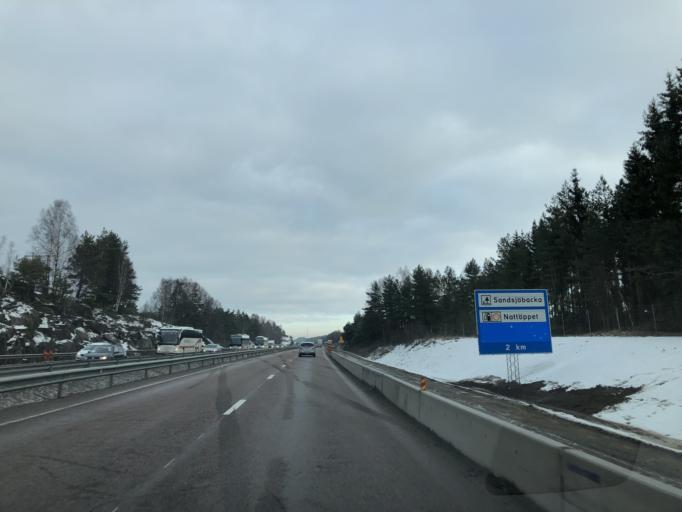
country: SE
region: Vaestra Goetaland
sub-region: Molndal
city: Lindome
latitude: 57.5298
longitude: 12.0495
